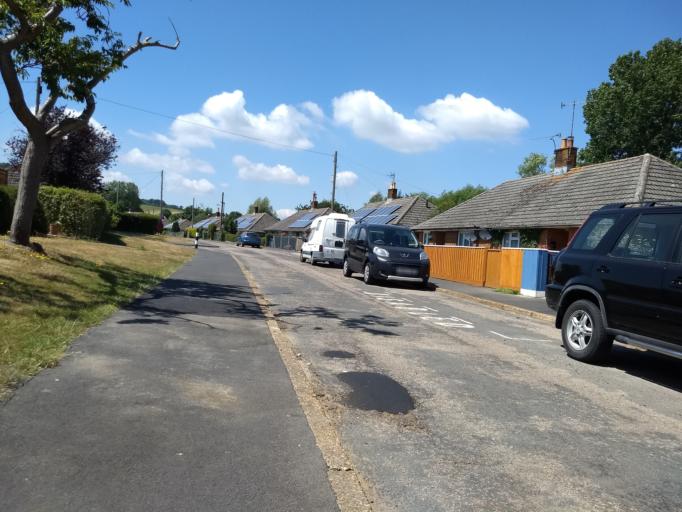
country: GB
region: England
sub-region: Isle of Wight
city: Brading
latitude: 50.6804
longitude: -1.1390
